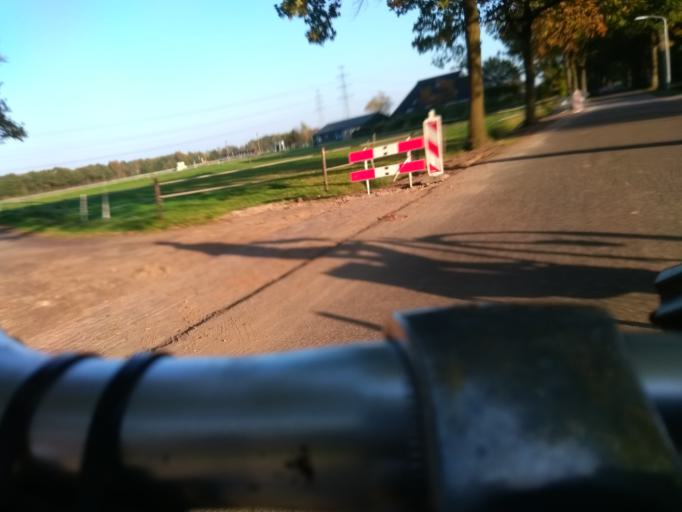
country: NL
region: Drenthe
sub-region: Gemeente Assen
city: Assen
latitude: 52.9783
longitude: 6.5212
